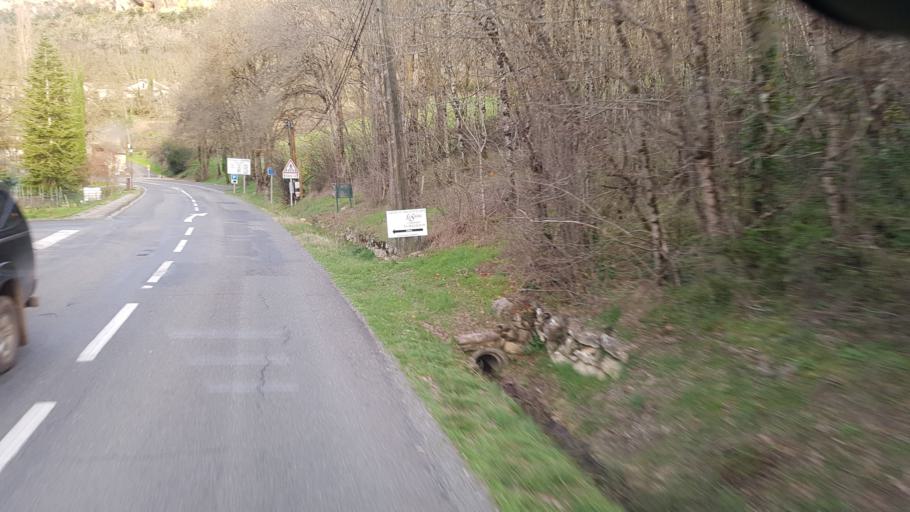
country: FR
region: Midi-Pyrenees
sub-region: Departement du Tarn-et-Garonne
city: Montricoux
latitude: 44.0023
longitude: 1.6926
